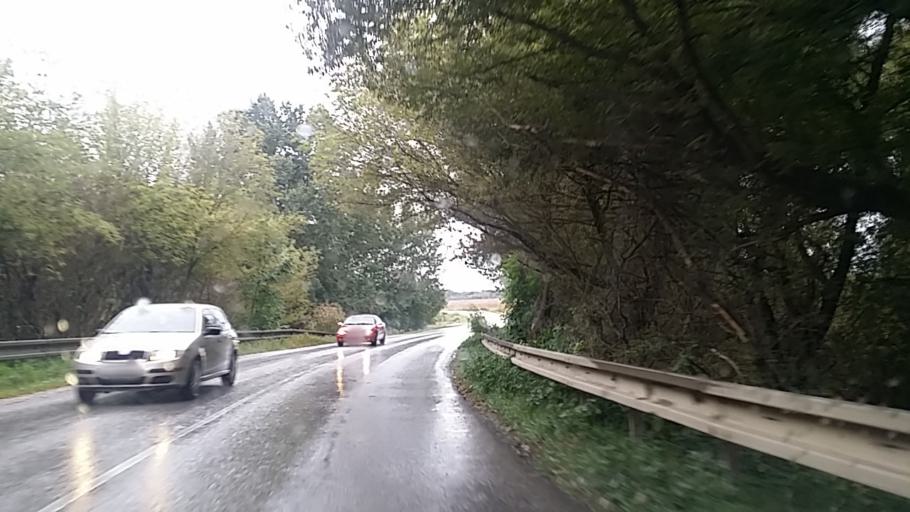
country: SK
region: Nitriansky
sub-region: Okres Nove Zamky
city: Sturovo
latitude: 47.8259
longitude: 18.7198
